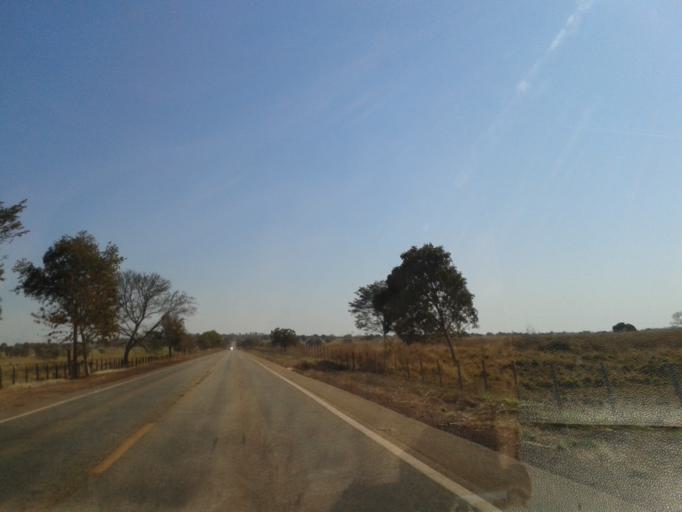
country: BR
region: Goias
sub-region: Mozarlandia
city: Mozarlandia
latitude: -14.7166
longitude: -50.5461
